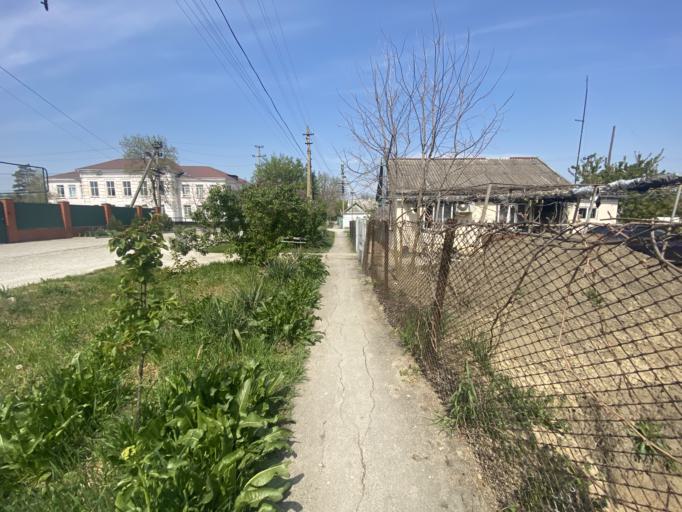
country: RU
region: Krasnodarskiy
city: Slavyansk-na-Kubani
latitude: 45.2675
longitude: 38.1228
